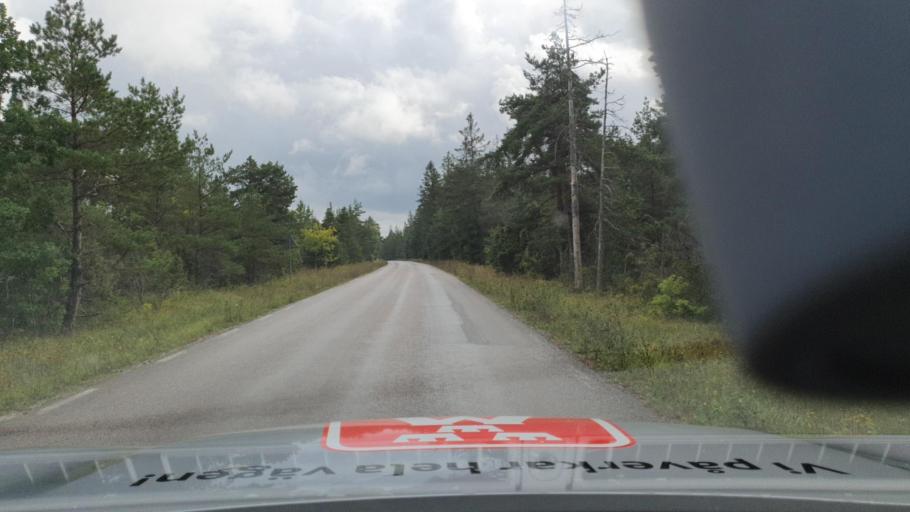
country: SE
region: Gotland
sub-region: Gotland
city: Slite
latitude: 57.7169
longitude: 18.7523
